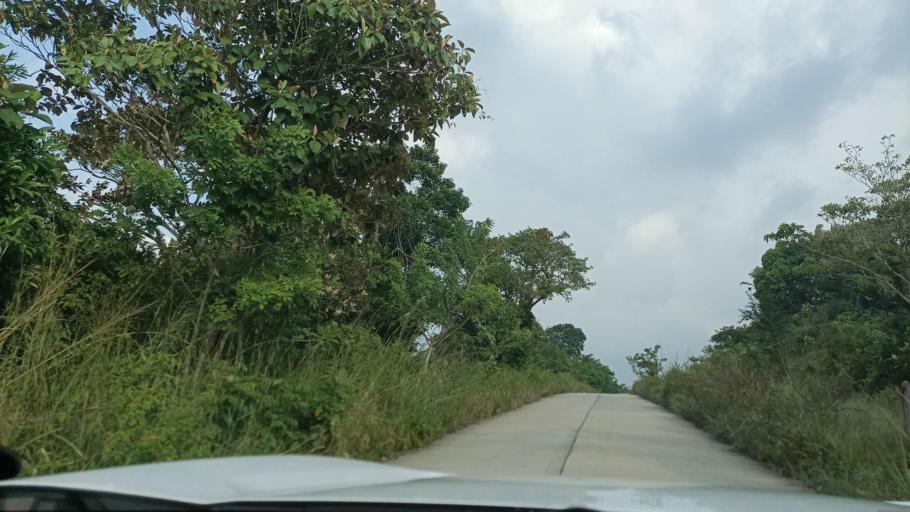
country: MX
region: Veracruz
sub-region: Moloacan
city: Tlacuilolapan
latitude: 18.0763
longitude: -94.2924
